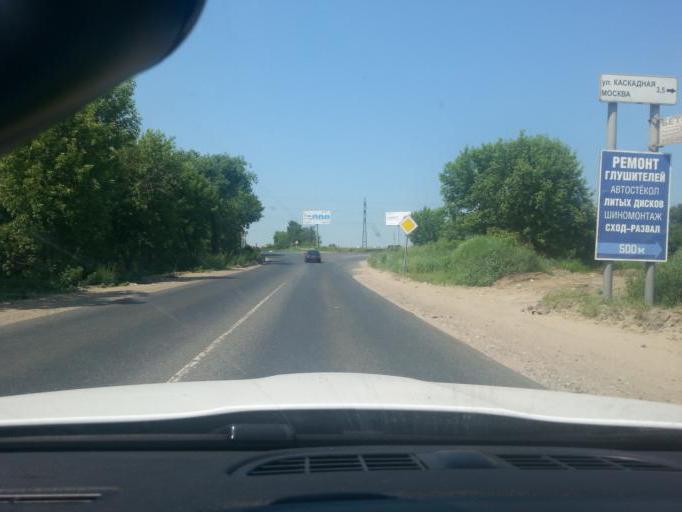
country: RU
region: Moscow
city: Nekrasovka
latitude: 55.7109
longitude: 37.9540
